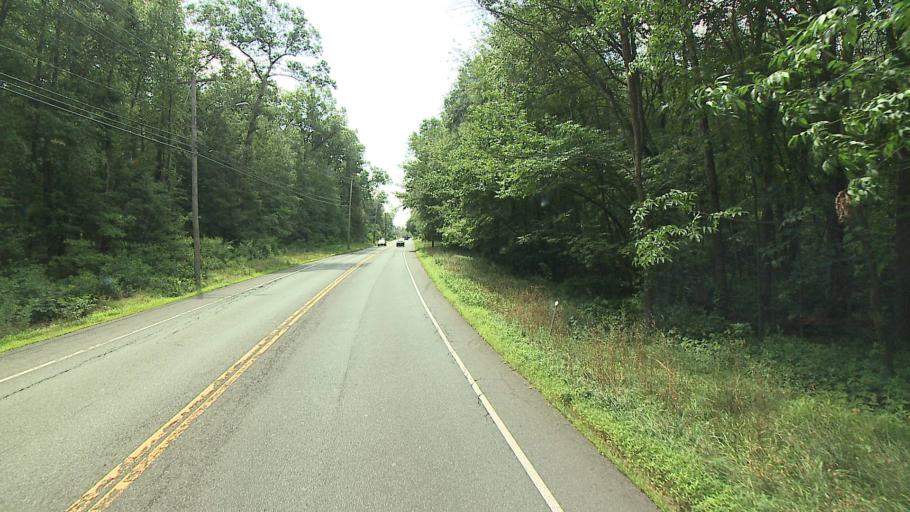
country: US
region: Connecticut
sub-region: Hartford County
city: Plainville
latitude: 41.7176
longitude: -72.8823
